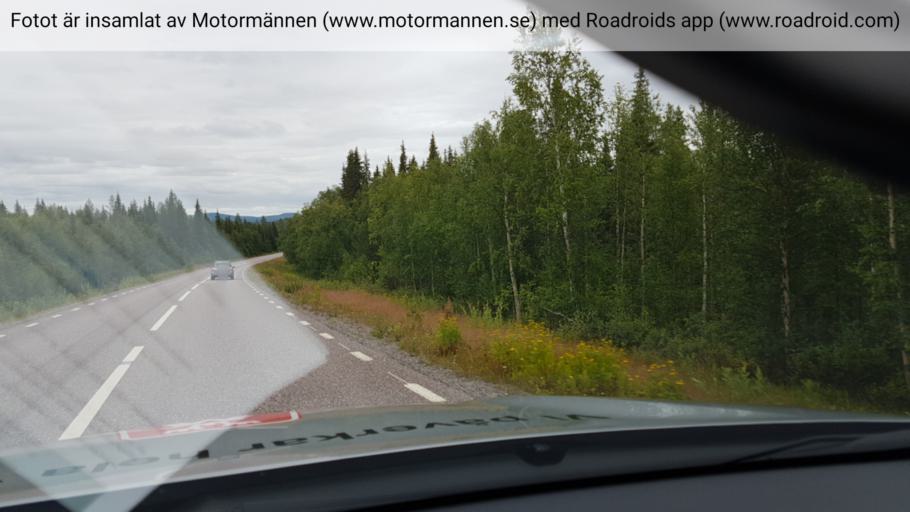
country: SE
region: Norrbotten
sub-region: Gallivare Kommun
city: Gaellivare
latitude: 67.0341
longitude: 21.7006
